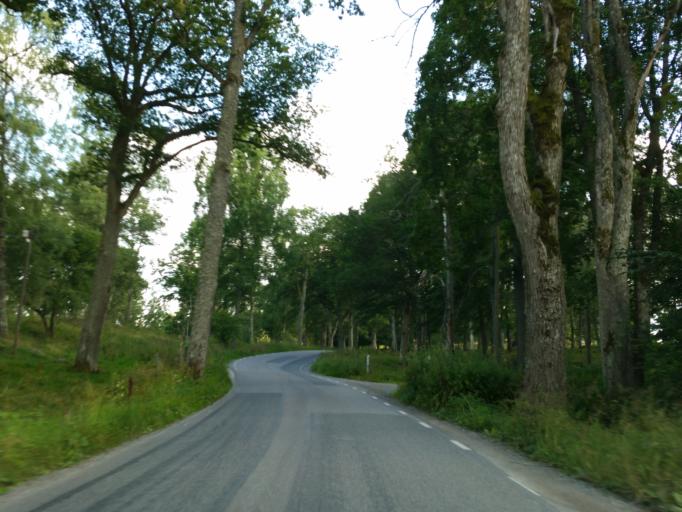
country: SE
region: Soedermanland
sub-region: Strangnas Kommun
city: Mariefred
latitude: 59.2356
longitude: 17.3032
